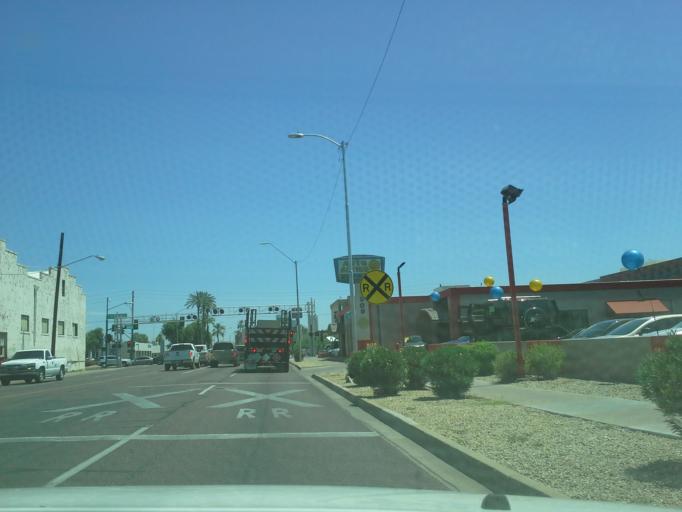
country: US
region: Arizona
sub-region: Maricopa County
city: Phoenix
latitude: 33.4512
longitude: -112.1013
